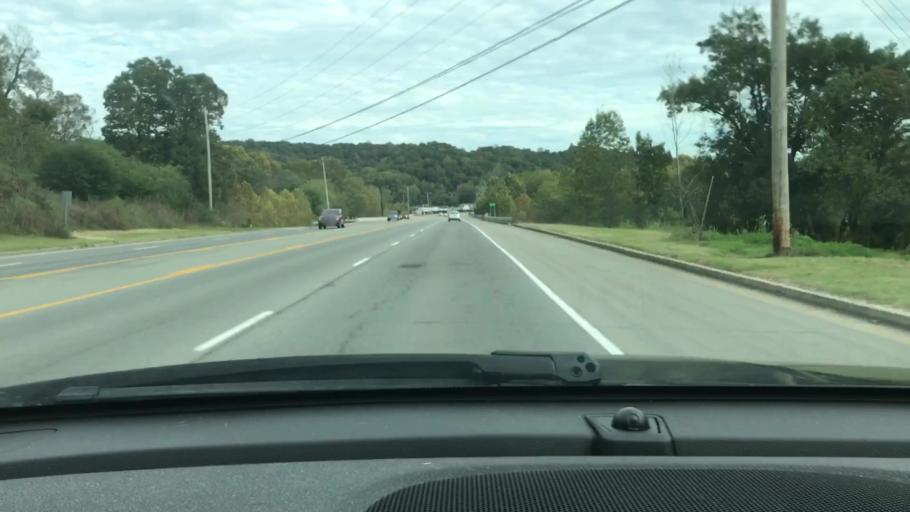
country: US
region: Tennessee
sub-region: Cheatham County
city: Ashland City
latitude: 36.2613
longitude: -87.0519
